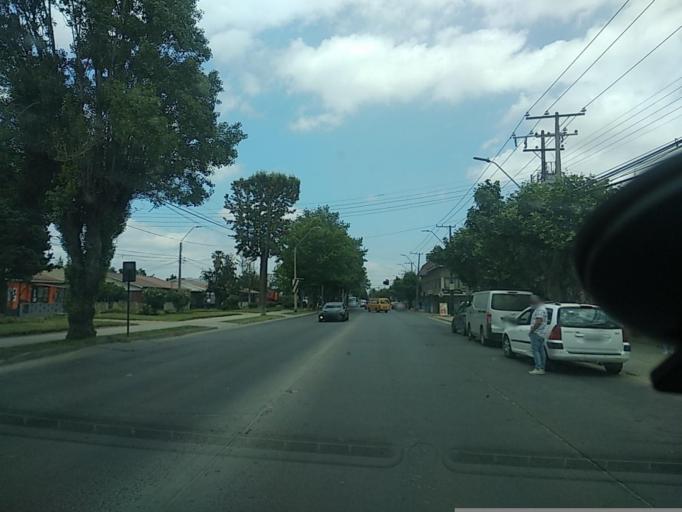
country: CL
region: Valparaiso
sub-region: Provincia de Marga Marga
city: Villa Alemana
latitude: -33.0449
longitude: -71.3867
